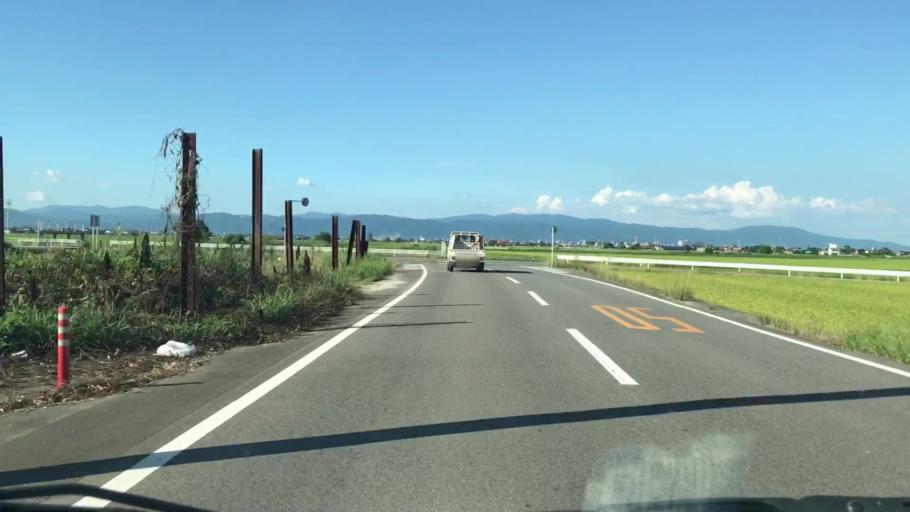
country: JP
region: Saga Prefecture
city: Saga-shi
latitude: 33.2065
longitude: 130.2685
